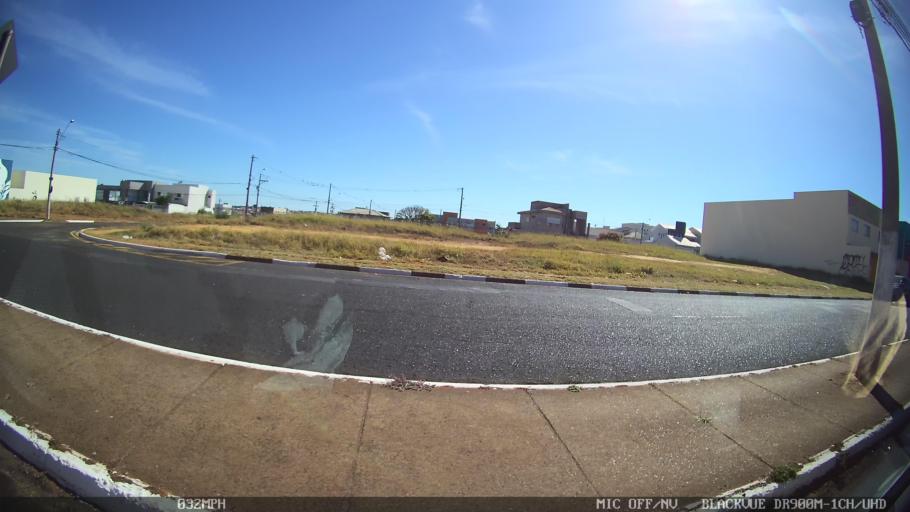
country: BR
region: Sao Paulo
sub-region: Franca
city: Franca
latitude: -20.5414
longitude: -47.3727
